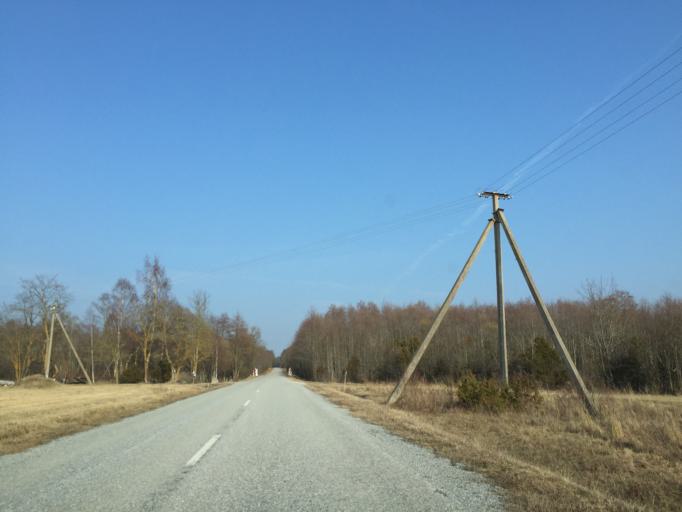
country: EE
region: Saare
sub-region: Orissaare vald
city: Orissaare
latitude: 58.5569
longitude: 23.3222
